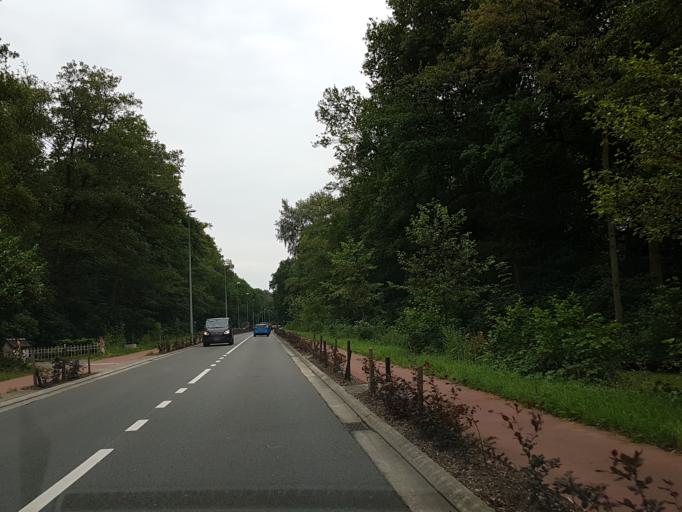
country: BE
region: Flanders
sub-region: Provincie Antwerpen
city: Schoten
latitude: 51.2605
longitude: 4.4762
